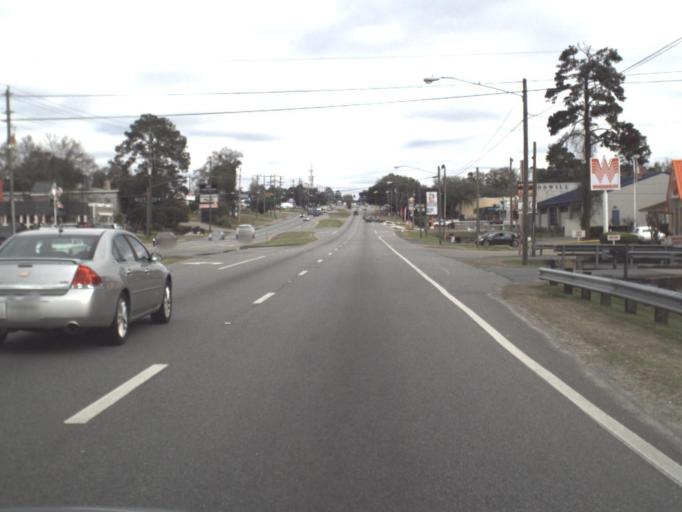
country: US
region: Florida
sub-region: Leon County
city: Tallahassee
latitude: 30.4769
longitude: -84.2981
